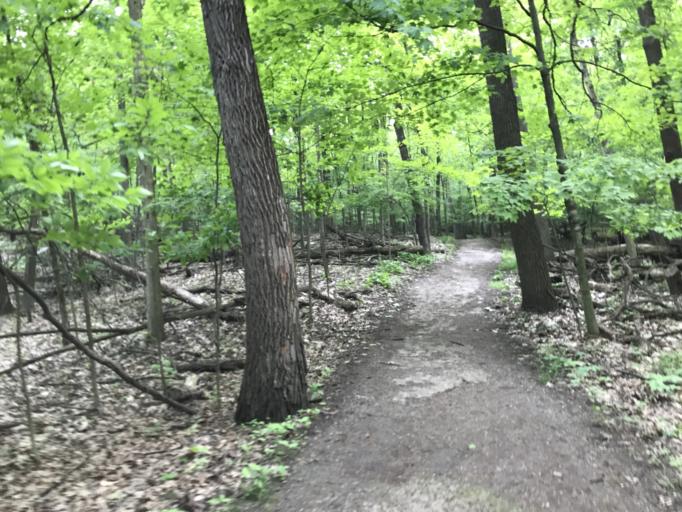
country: US
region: Michigan
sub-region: Oakland County
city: Farmington Hills
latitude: 42.4764
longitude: -83.3880
